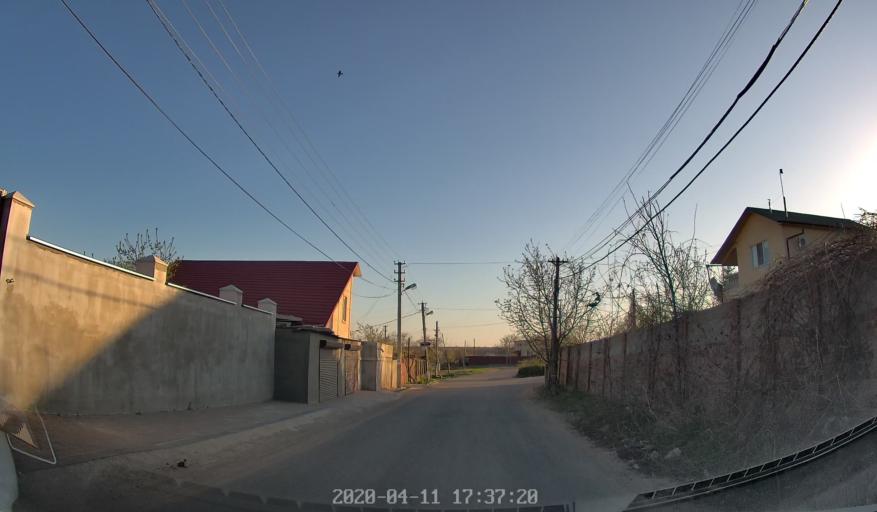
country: MD
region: Laloveni
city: Ialoveni
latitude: 46.9796
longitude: 28.8014
